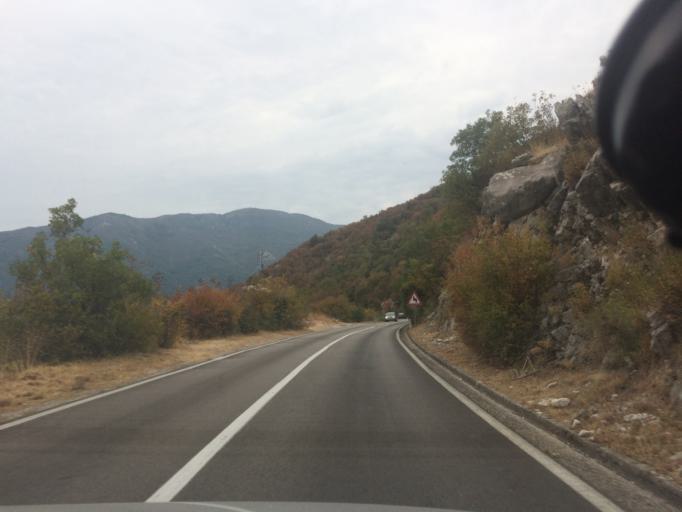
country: ME
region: Kotor
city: Risan
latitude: 42.5088
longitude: 18.6784
